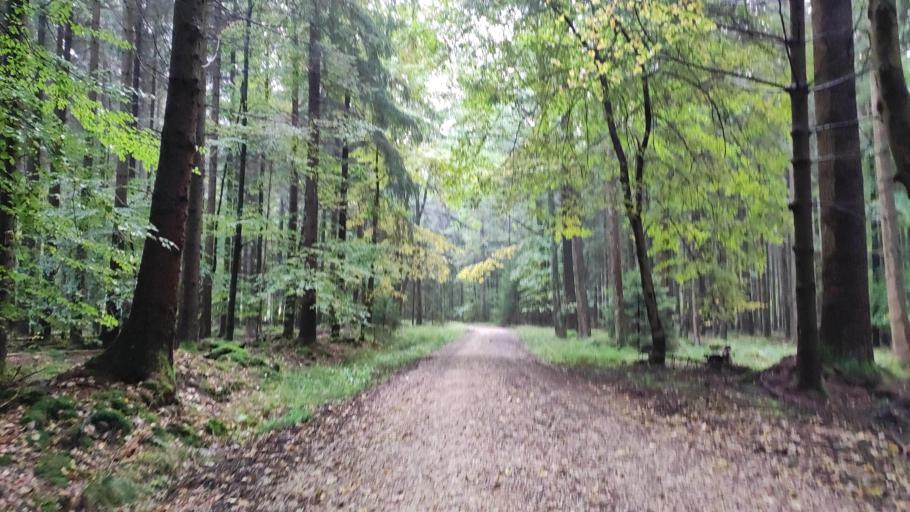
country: DE
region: Bavaria
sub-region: Swabia
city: Welden
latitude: 48.4244
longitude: 10.6400
